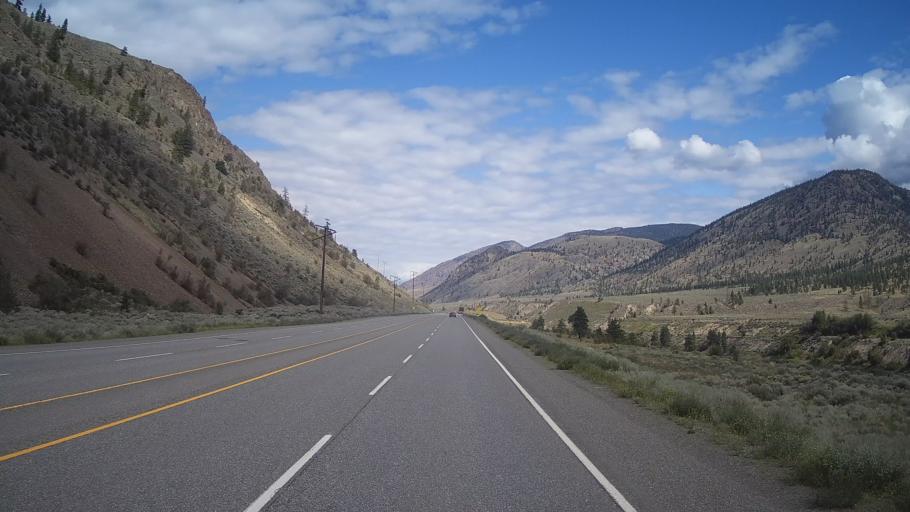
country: CA
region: British Columbia
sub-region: Thompson-Nicola Regional District
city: Ashcroft
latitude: 50.5243
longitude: -121.2856
